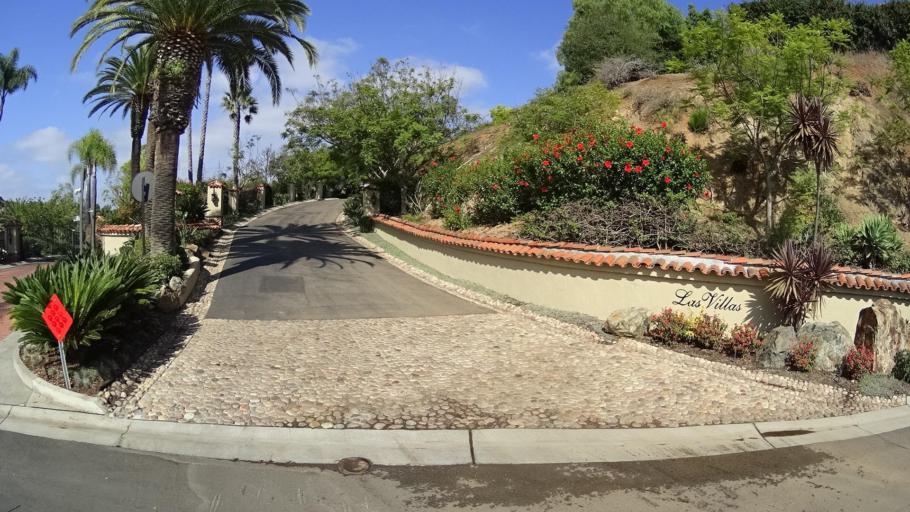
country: US
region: California
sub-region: San Diego County
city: Rancho Santa Fe
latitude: 33.0511
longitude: -117.2002
